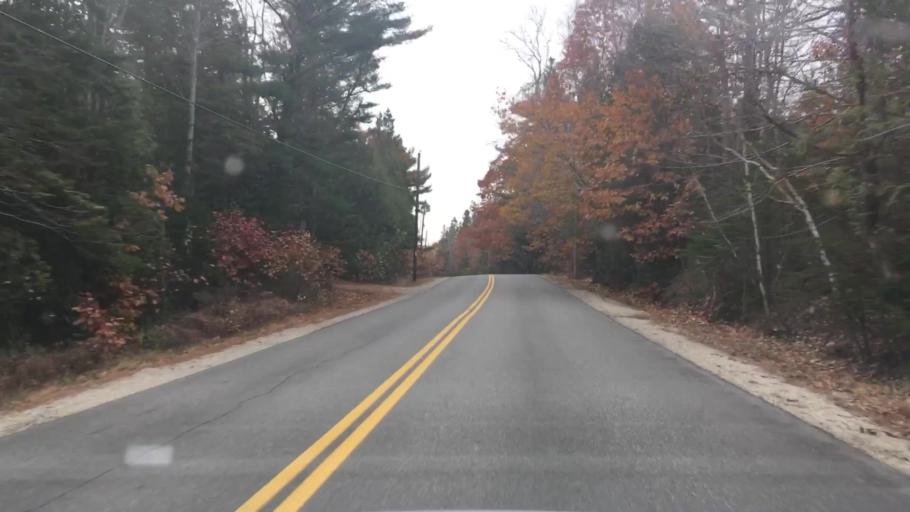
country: US
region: Maine
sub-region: Hancock County
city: Penobscot
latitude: 44.4588
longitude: -68.6378
